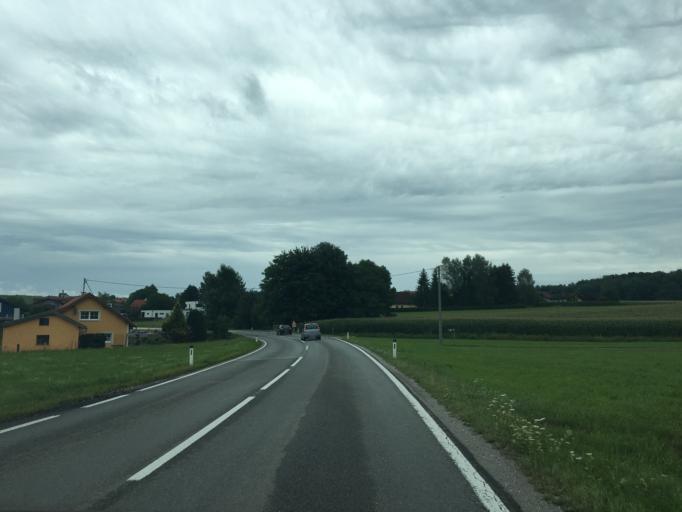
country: AT
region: Salzburg
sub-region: Politischer Bezirk Salzburg-Umgebung
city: Dorfbeuern
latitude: 48.0357
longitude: 12.9848
